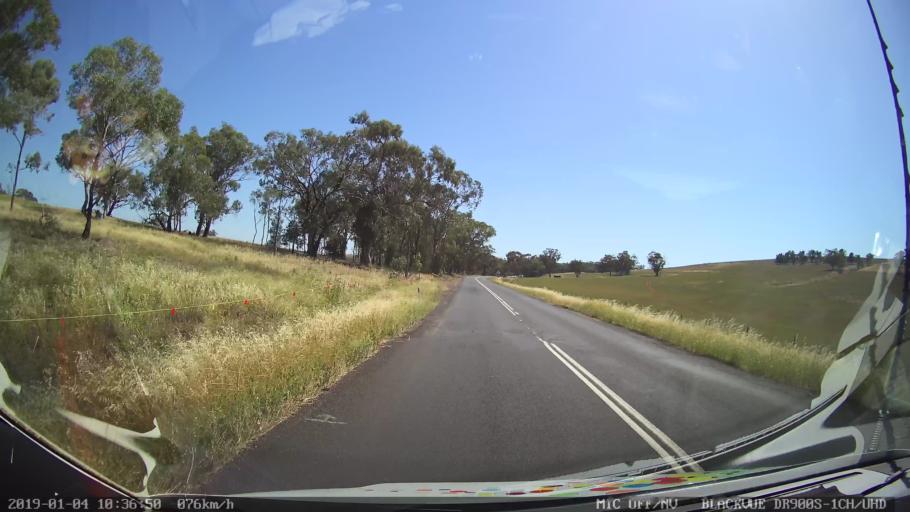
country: AU
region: New South Wales
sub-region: Cabonne
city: Canowindra
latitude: -33.3007
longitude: 148.6885
